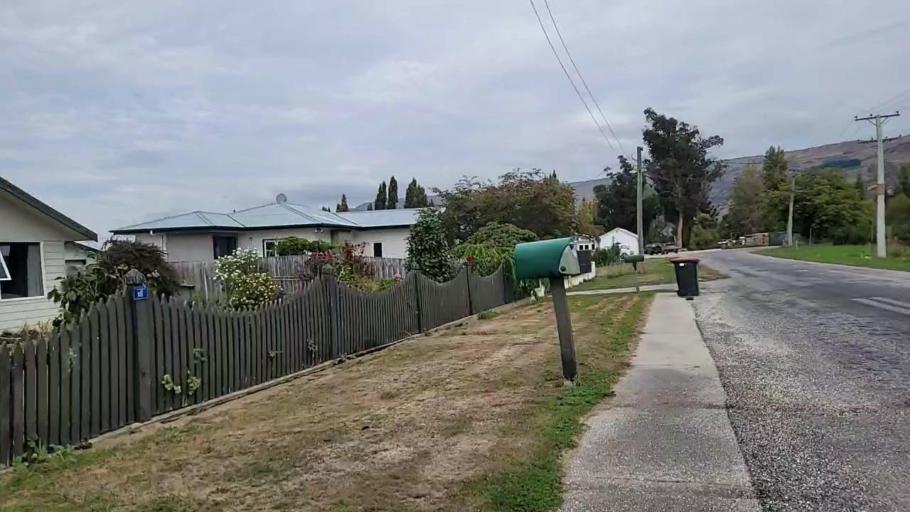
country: NZ
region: Otago
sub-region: Queenstown-Lakes District
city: Kingston
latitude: -45.4816
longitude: 169.3124
